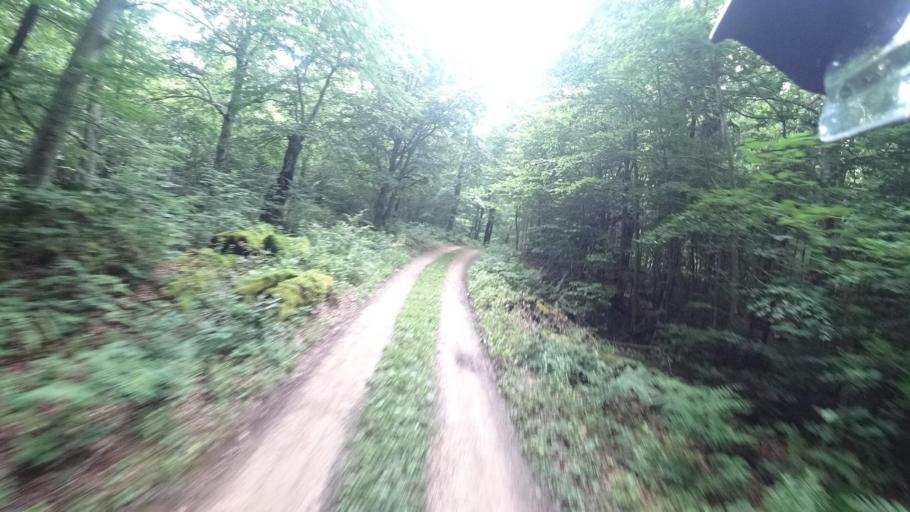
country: HR
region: Licko-Senjska
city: Jezerce
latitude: 44.7831
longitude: 15.6446
